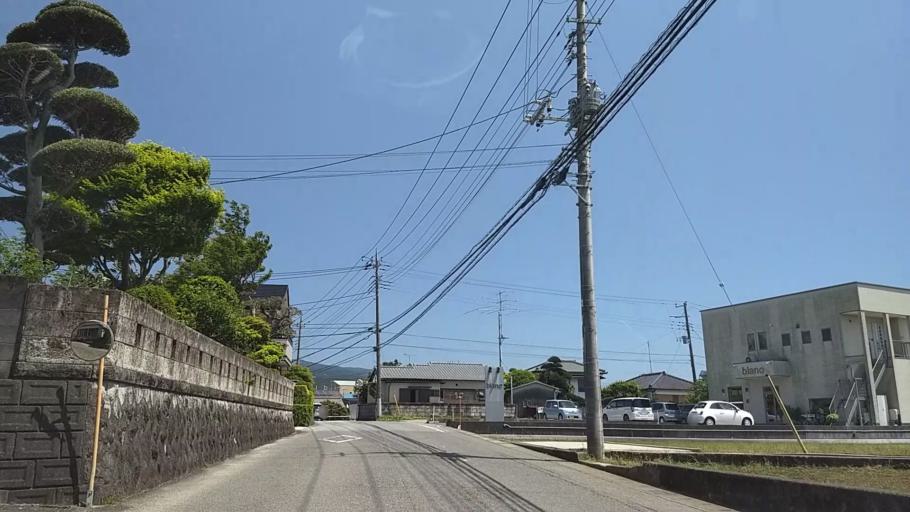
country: JP
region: Shizuoka
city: Mishima
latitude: 35.2006
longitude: 138.9095
